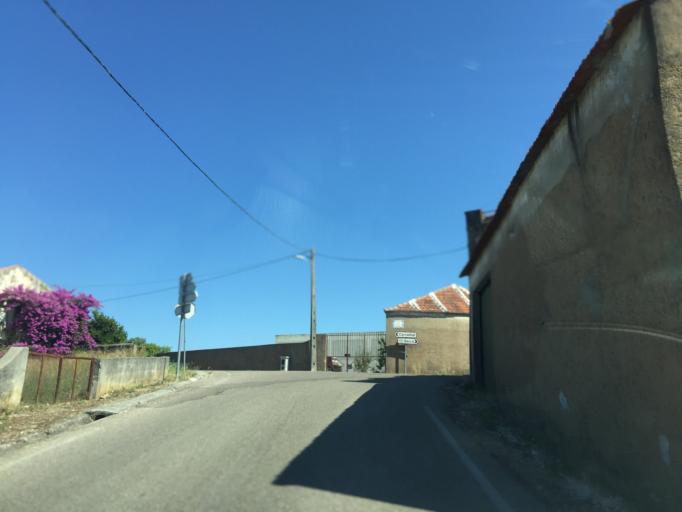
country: PT
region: Santarem
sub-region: Ferreira do Zezere
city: Ferreira do Zezere
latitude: 39.5982
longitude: -8.3013
